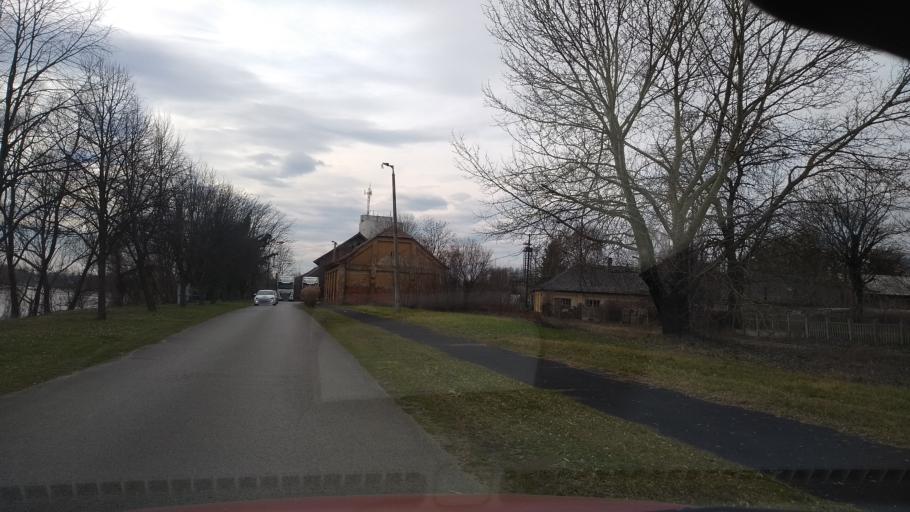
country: HU
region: Somogy
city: Barcs
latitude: 45.9515
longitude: 17.4433
